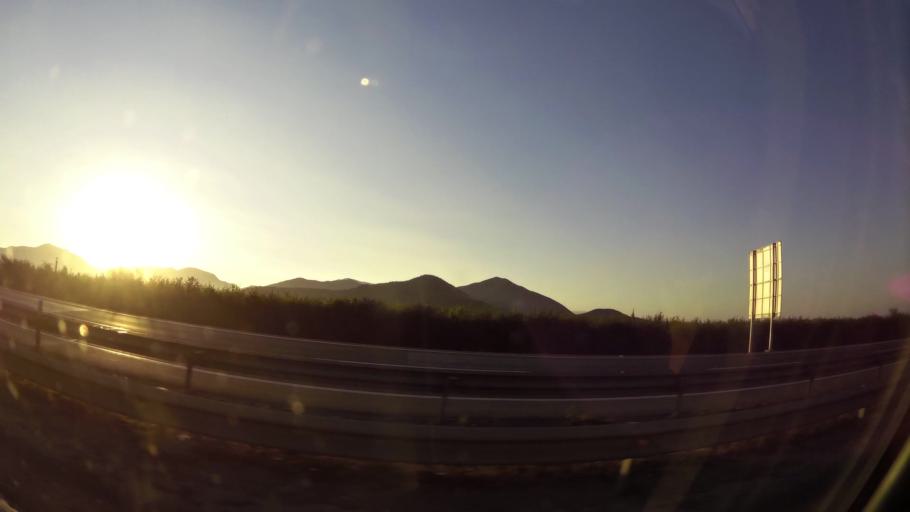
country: CL
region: Santiago Metropolitan
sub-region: Provincia de Santiago
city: Lo Prado
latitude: -33.5011
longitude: -70.7973
